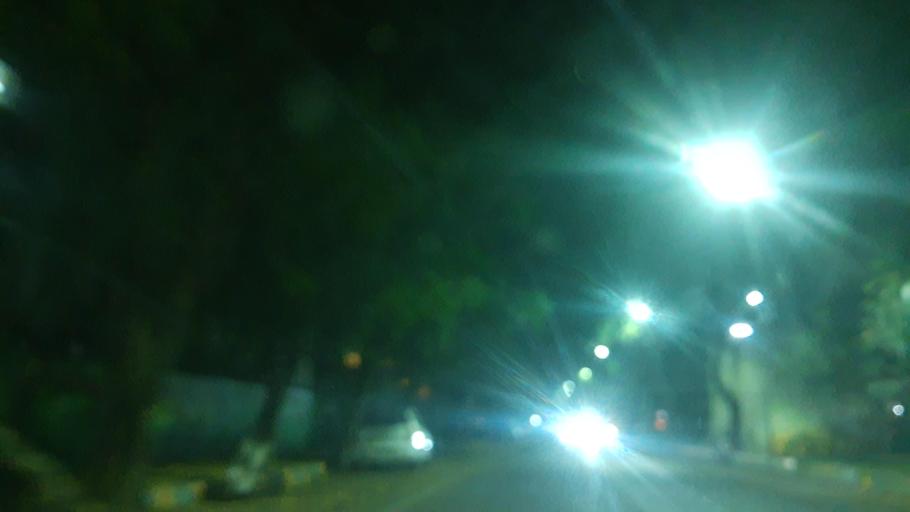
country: IN
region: Maharashtra
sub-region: Thane
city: Thane
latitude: 19.1909
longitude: 72.9636
